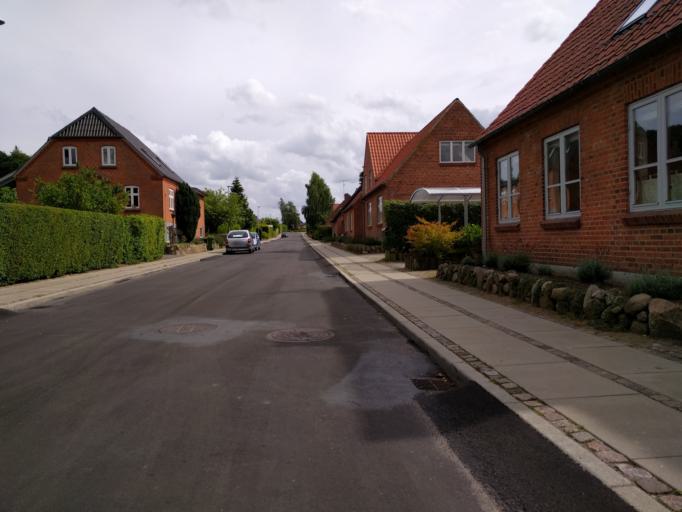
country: DK
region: Central Jutland
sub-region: Skanderborg Kommune
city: Ry
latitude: 56.0887
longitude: 9.7676
